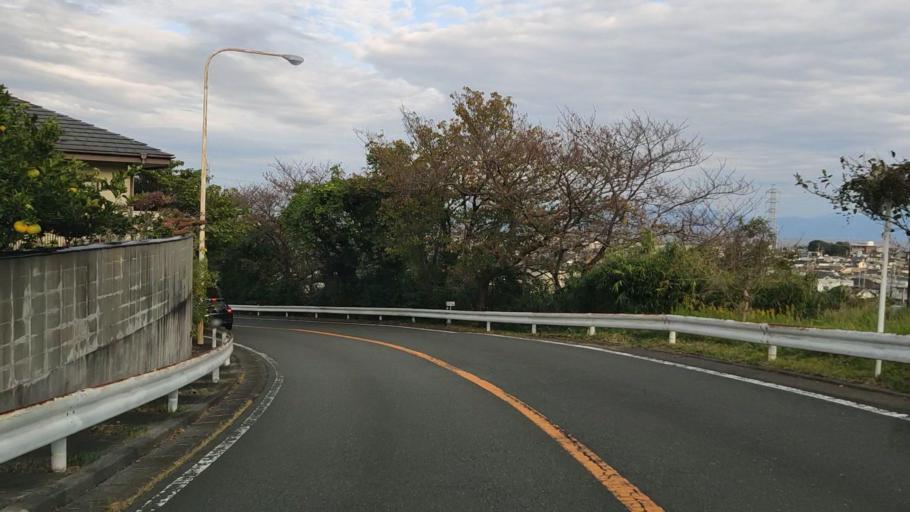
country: JP
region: Shizuoka
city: Shizuoka-shi
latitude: 34.9791
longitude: 138.4917
